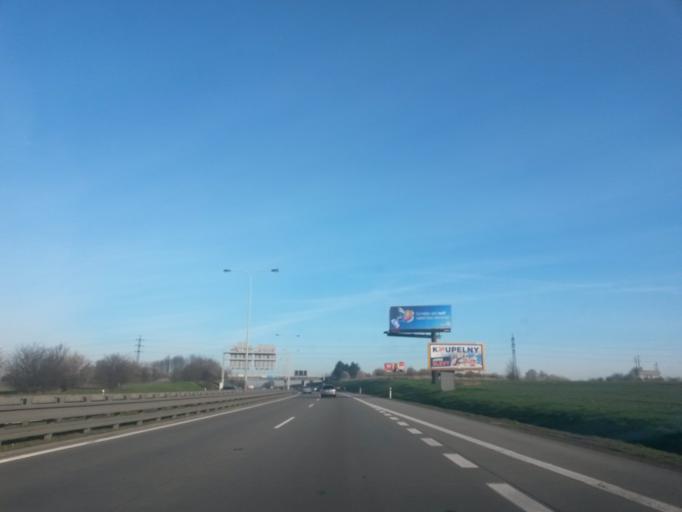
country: CZ
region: Central Bohemia
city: Cernosice
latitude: 50.0181
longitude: 14.3373
